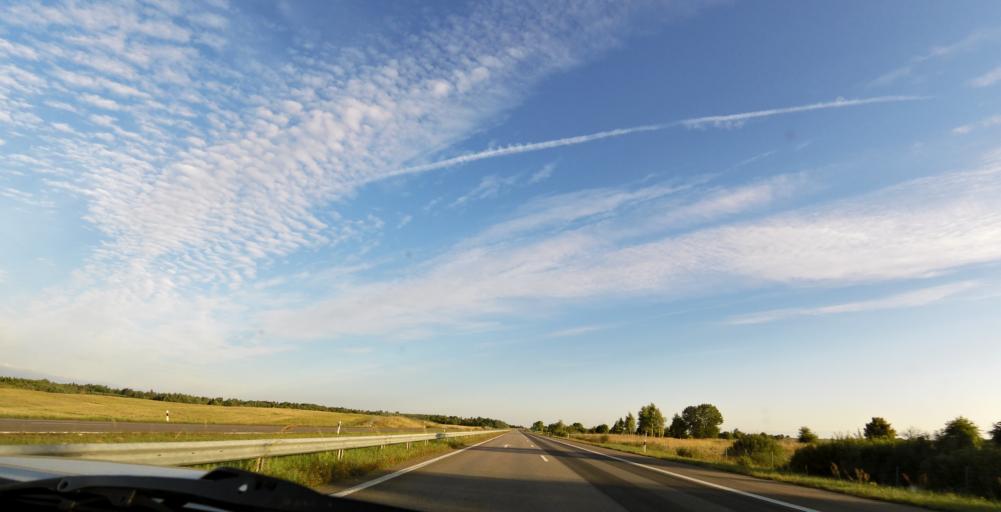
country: LT
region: Vilnius County
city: Ukmerge
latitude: 55.1653
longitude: 24.8173
